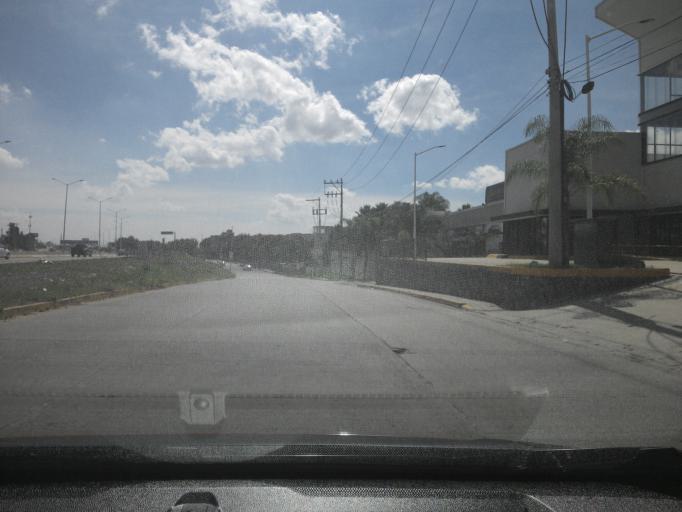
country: MX
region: Jalisco
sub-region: Tlajomulco de Zuniga
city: Altus Bosques
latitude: 20.5866
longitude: -103.3828
